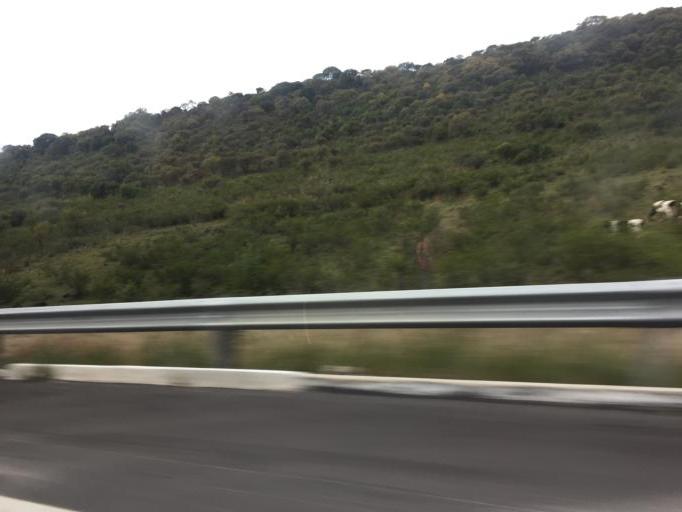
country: MX
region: Jalisco
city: Ocotlan
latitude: 20.4149
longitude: -102.7473
